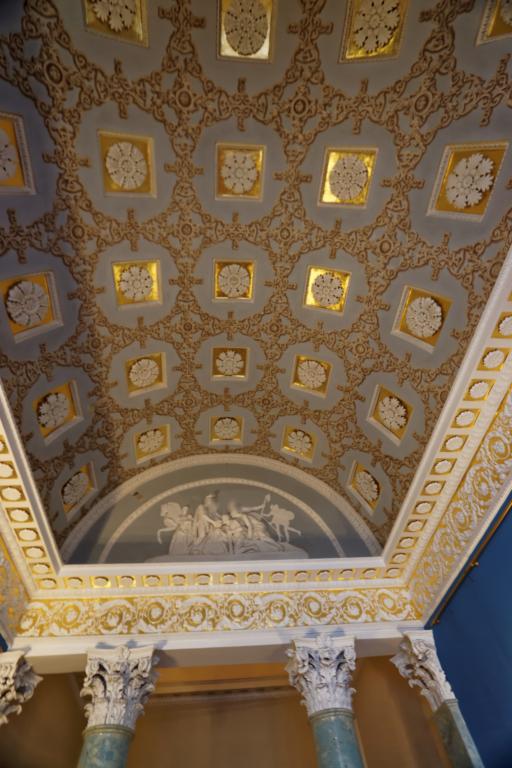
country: RU
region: St.-Petersburg
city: Saint Petersburg
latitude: 59.9355
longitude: 30.3201
